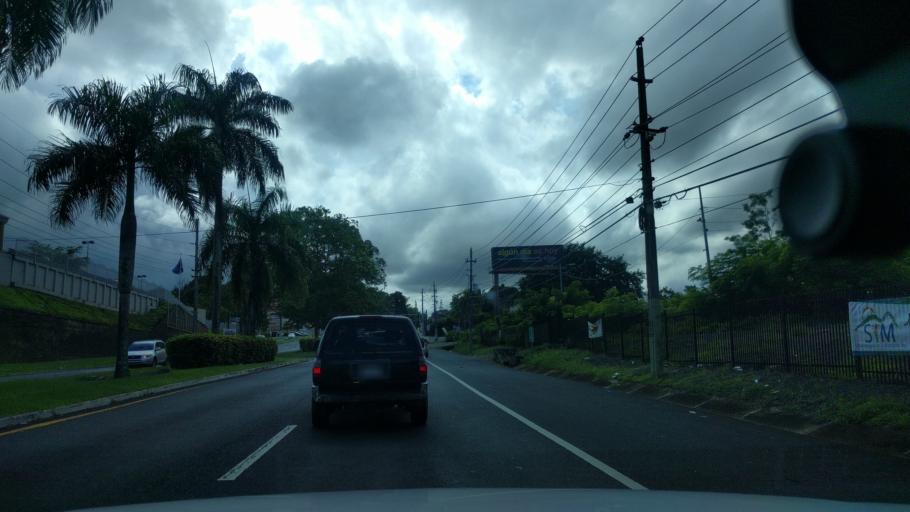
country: PR
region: Toa Alta
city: Pajaros
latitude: 18.3632
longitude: -66.1891
